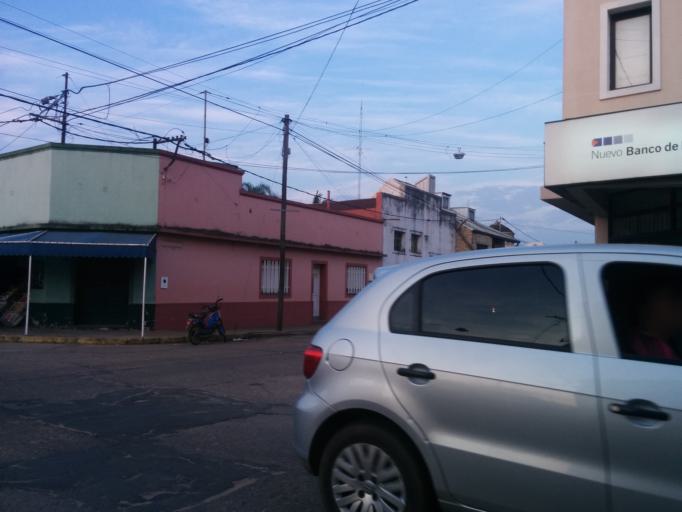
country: AR
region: Entre Rios
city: Concordia
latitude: -31.3858
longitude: -58.0184
